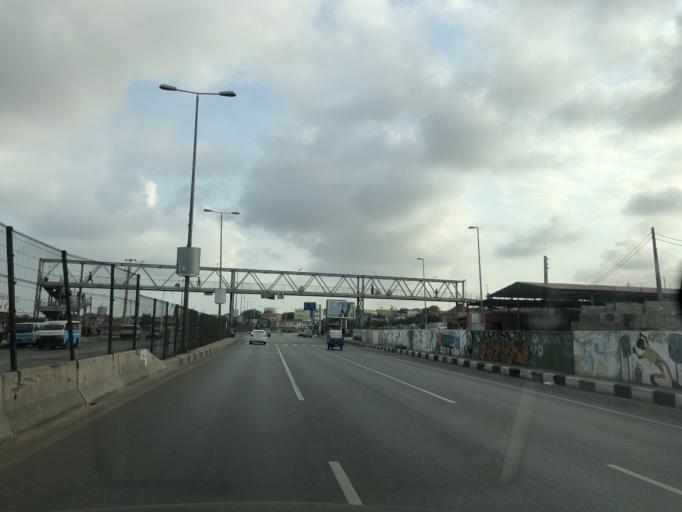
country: AO
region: Luanda
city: Luanda
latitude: -8.8533
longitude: 13.2200
